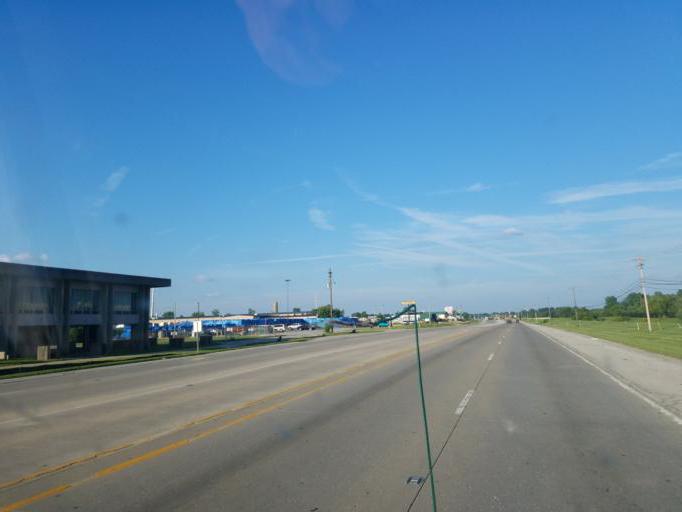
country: US
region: Kentucky
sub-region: Jefferson County
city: Heritage Creek
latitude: 38.1307
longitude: -85.7335
